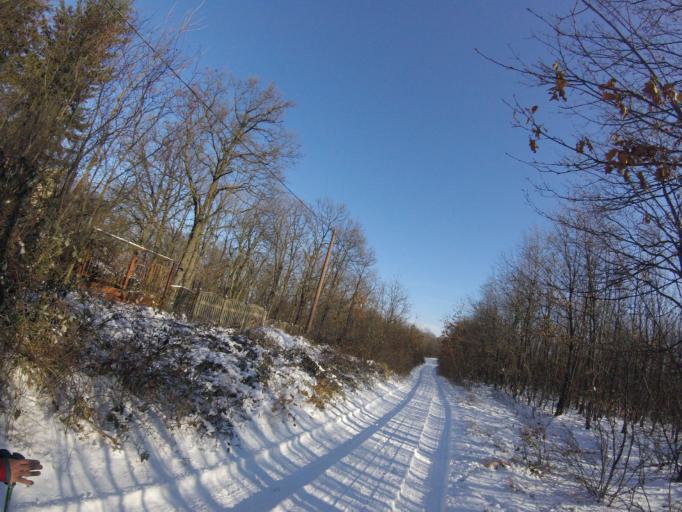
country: HU
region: Pest
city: Kismaros
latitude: 47.8385
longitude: 18.9869
